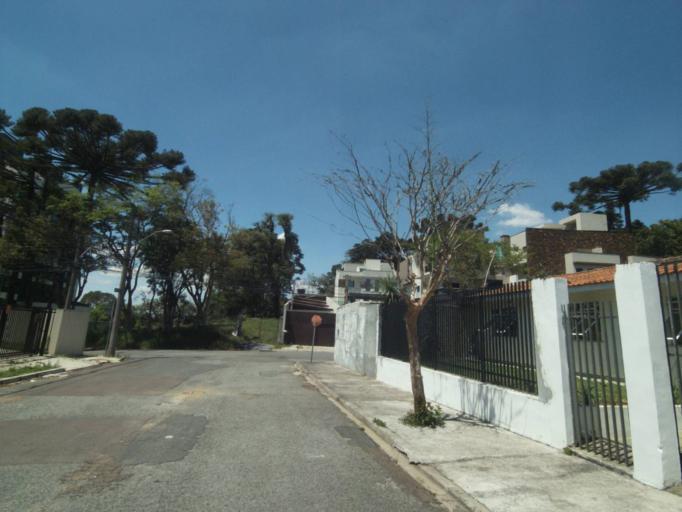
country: BR
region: Parana
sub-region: Curitiba
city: Curitiba
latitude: -25.3858
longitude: -49.2308
